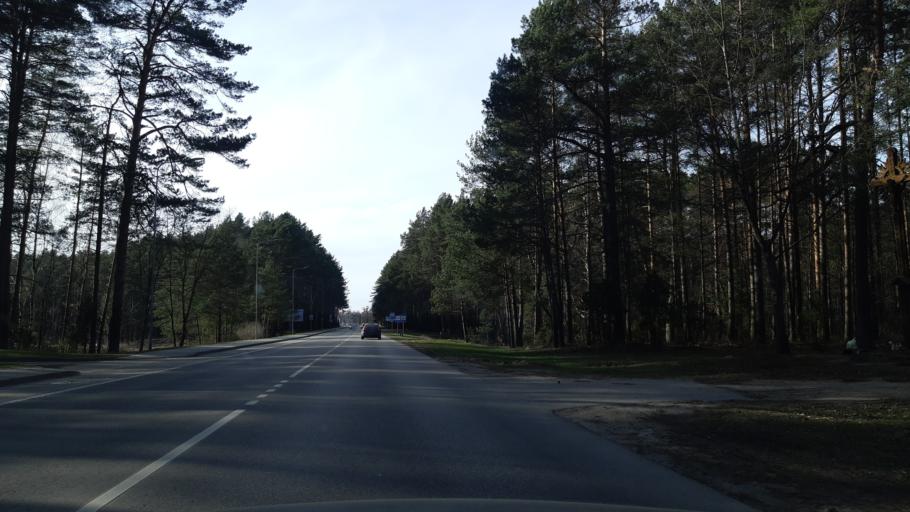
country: LT
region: Alytaus apskritis
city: Druskininkai
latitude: 54.0082
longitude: 23.9994
